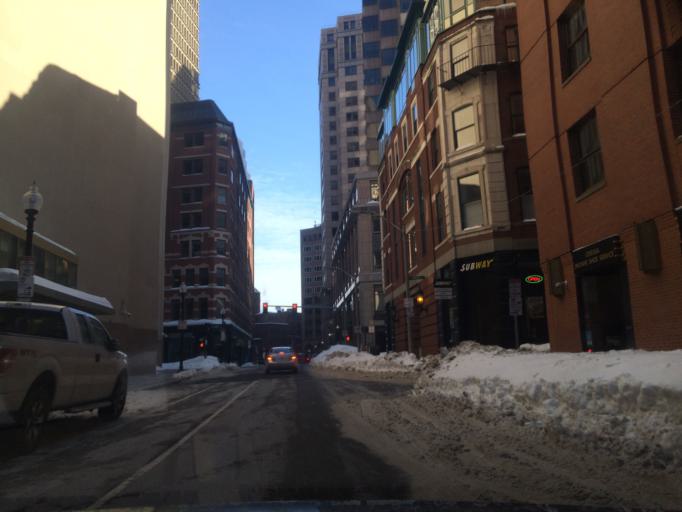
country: US
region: Massachusetts
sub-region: Suffolk County
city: Boston
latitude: 42.3546
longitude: -71.0547
